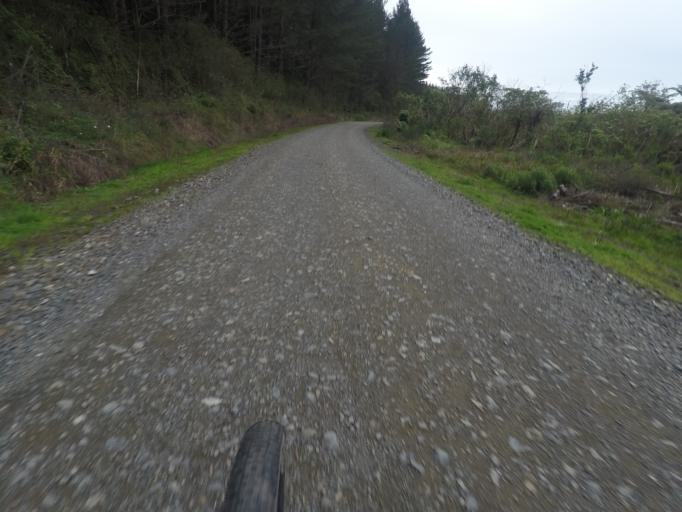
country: NZ
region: Auckland
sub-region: Auckland
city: Muriwai Beach
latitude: -36.7495
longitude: 174.5751
